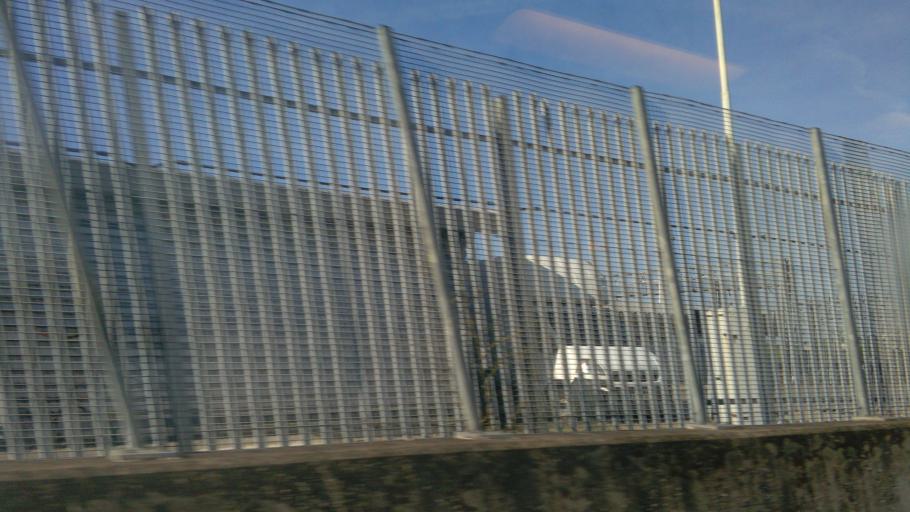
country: GB
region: England
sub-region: Kent
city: Hythe
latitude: 51.0926
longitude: 1.1065
